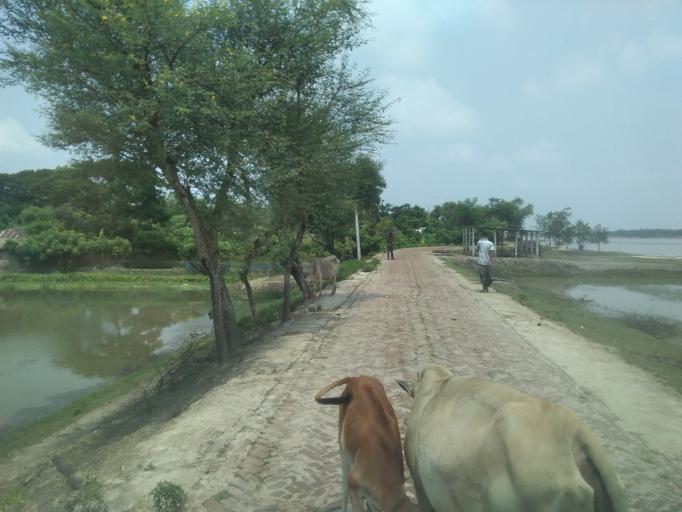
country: BD
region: Khulna
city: Phultala
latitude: 22.6414
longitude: 89.4244
